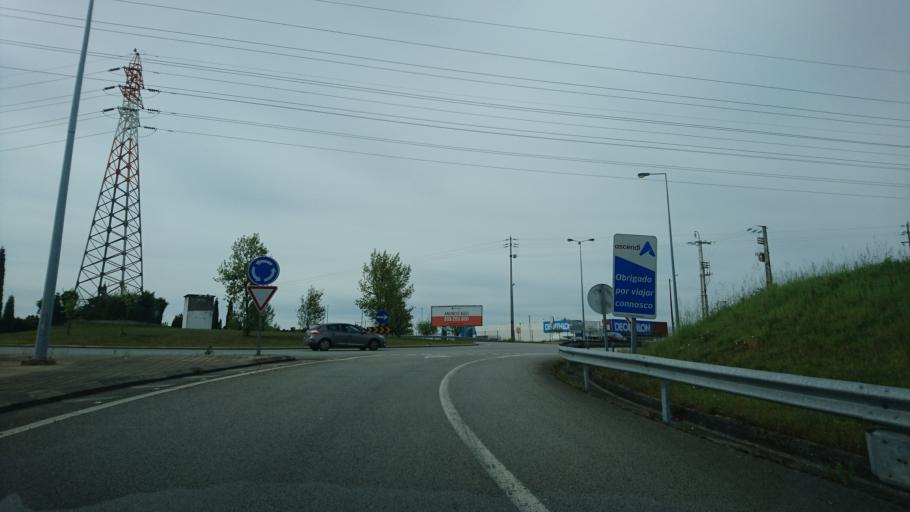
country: PT
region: Aveiro
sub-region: Aveiro
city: Eixo
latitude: 40.6474
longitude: -8.5982
